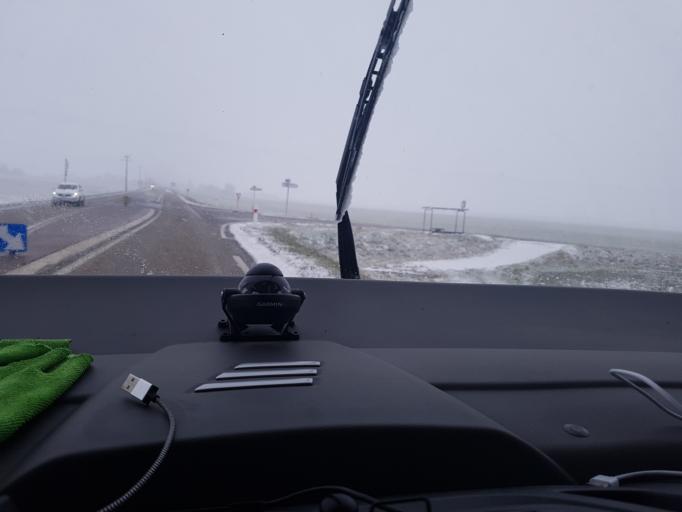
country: FR
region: Lorraine
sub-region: Departement de la Moselle
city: Chateau-Salins
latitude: 48.8693
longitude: 6.4243
